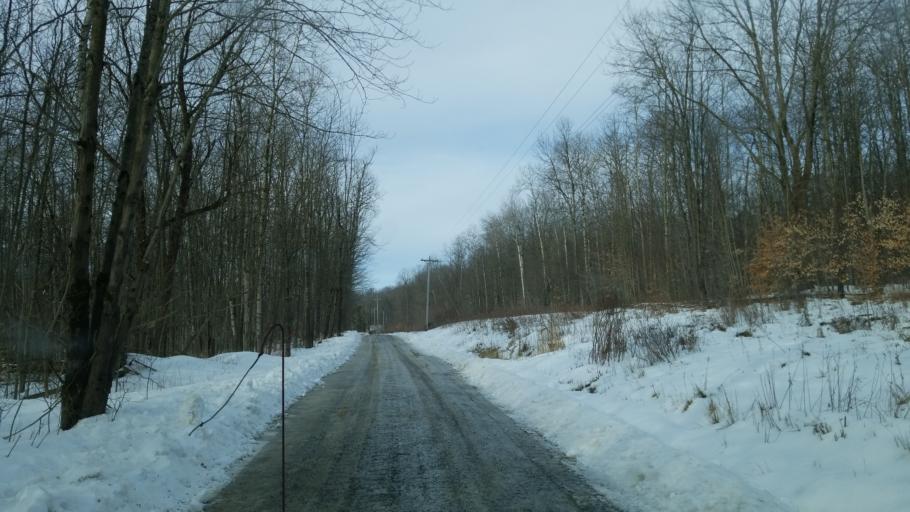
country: US
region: Pennsylvania
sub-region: Tioga County
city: Westfield
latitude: 41.9599
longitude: -77.7215
